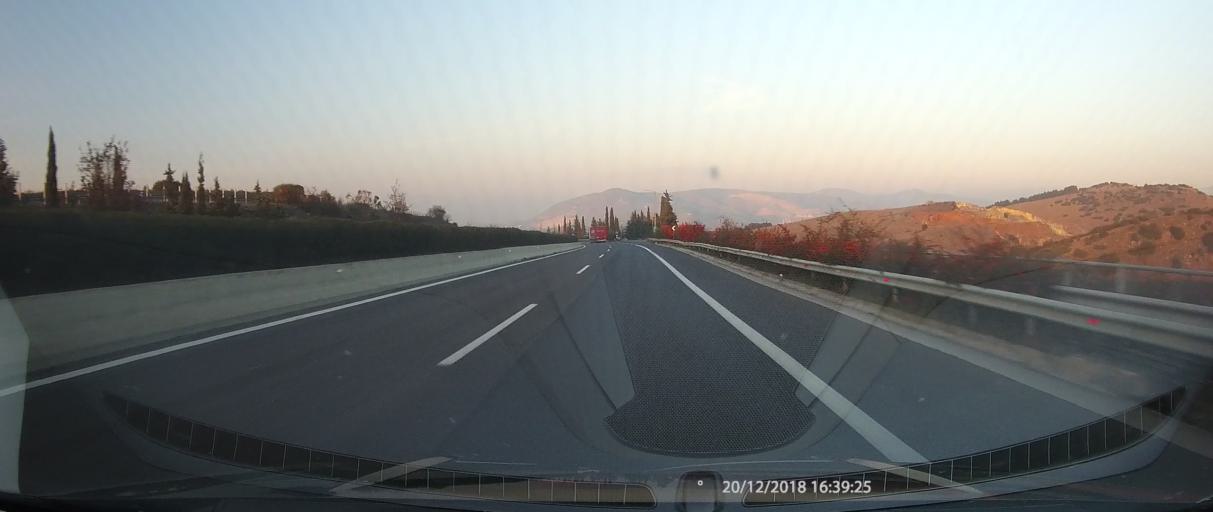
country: GR
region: Thessaly
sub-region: Nomos Magnisias
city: Velestino
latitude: 39.3580
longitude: 22.7734
